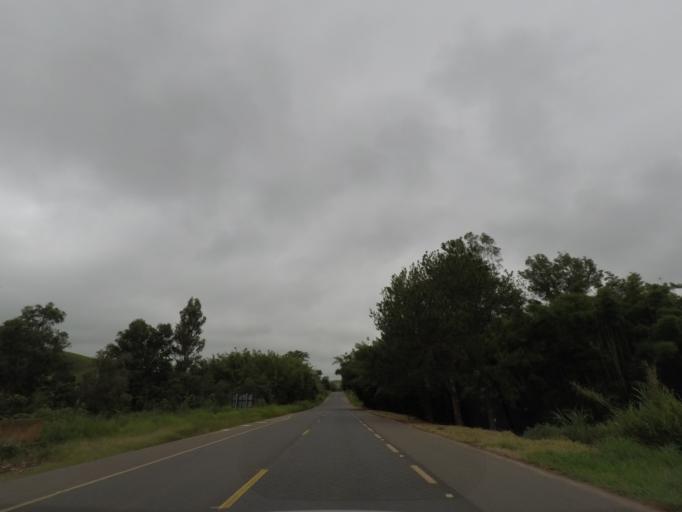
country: BR
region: Sao Paulo
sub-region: Cunha
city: Cunha
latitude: -22.9856
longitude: -45.0434
